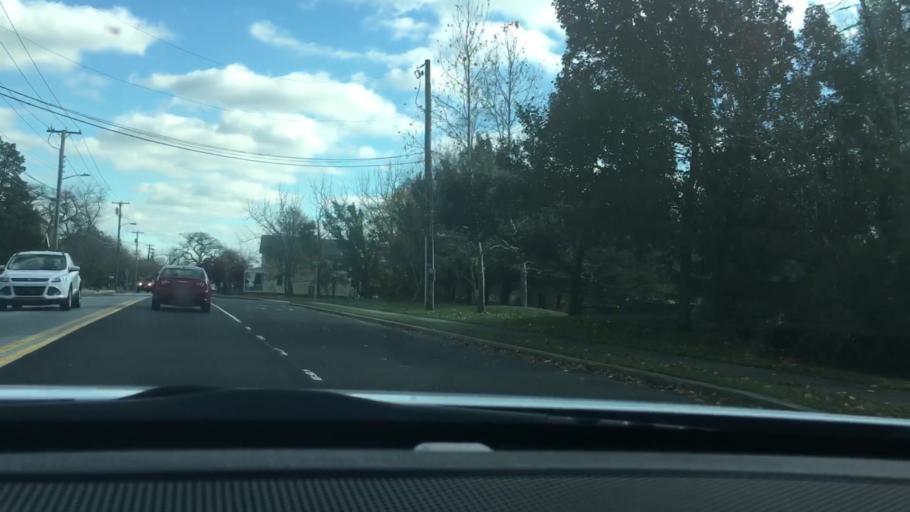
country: US
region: New Jersey
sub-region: Atlantic County
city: Northfield
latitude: 39.3751
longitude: -74.5706
